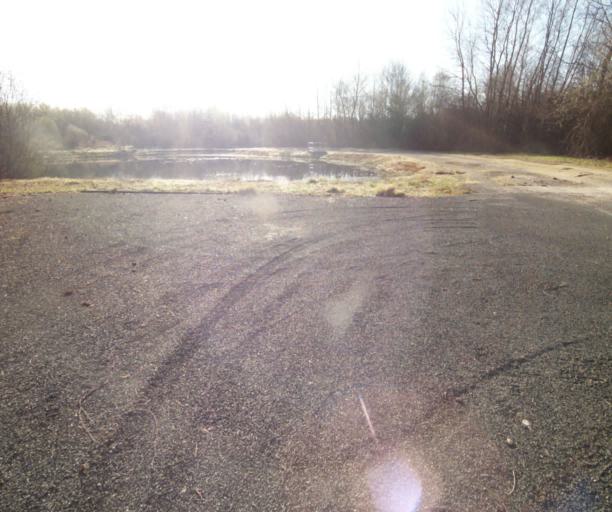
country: FR
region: Limousin
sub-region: Departement de la Correze
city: Correze
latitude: 45.3333
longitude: 1.9108
